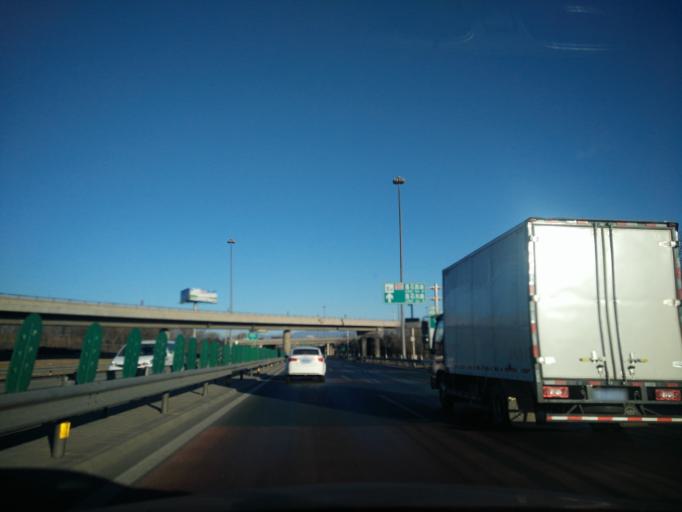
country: CN
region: Beijing
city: Fengtai
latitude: 39.8418
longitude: 116.2213
